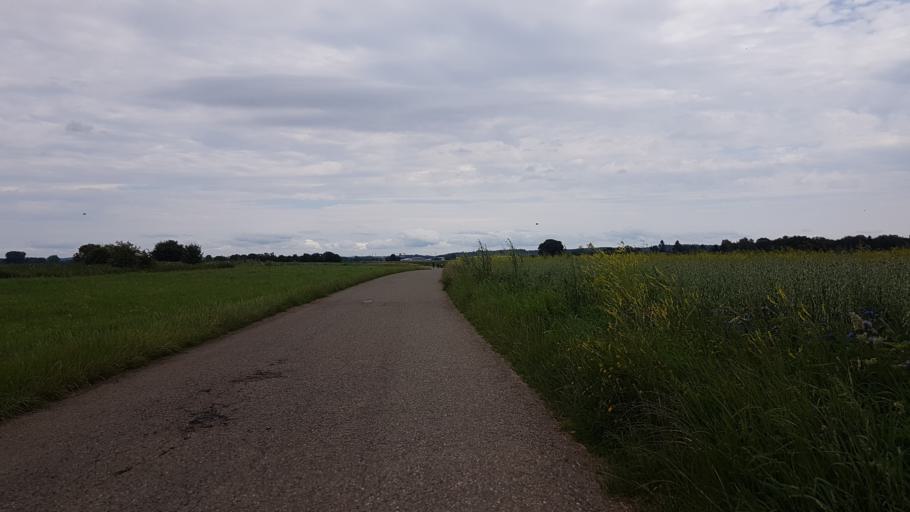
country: DE
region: Baden-Wuerttemberg
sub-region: Tuebingen Region
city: Mengen
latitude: 48.0609
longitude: 9.3537
